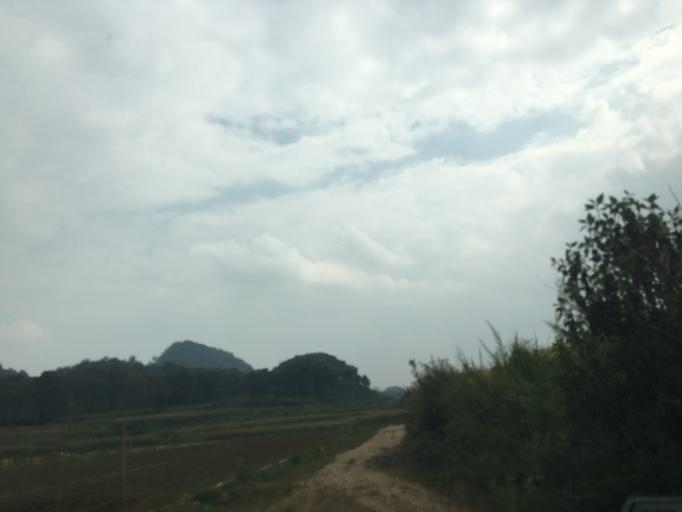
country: CN
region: Guangxi Zhuangzu Zizhiqu
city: Xinzhou
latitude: 25.4918
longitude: 105.6522
